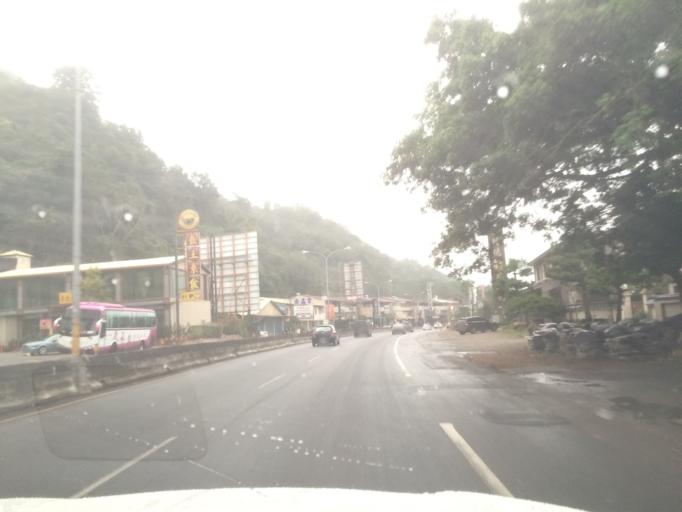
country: TW
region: Taiwan
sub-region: Nantou
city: Puli
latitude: 23.9660
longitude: 120.9344
